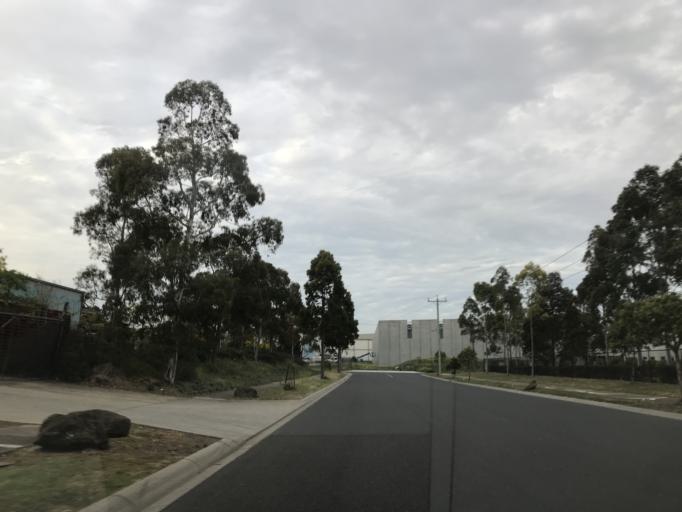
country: AU
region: Victoria
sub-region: Brimbank
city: Derrimut
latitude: -37.8105
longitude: 144.7827
